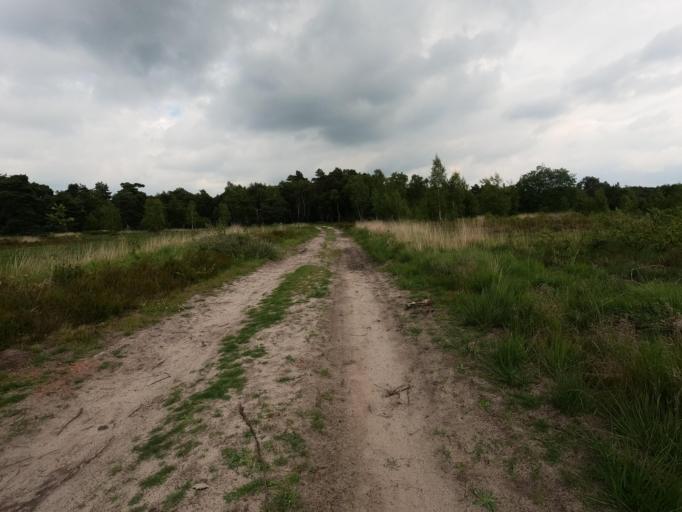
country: BE
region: Flanders
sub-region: Provincie Antwerpen
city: Kalmthout
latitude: 51.3560
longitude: 4.4963
